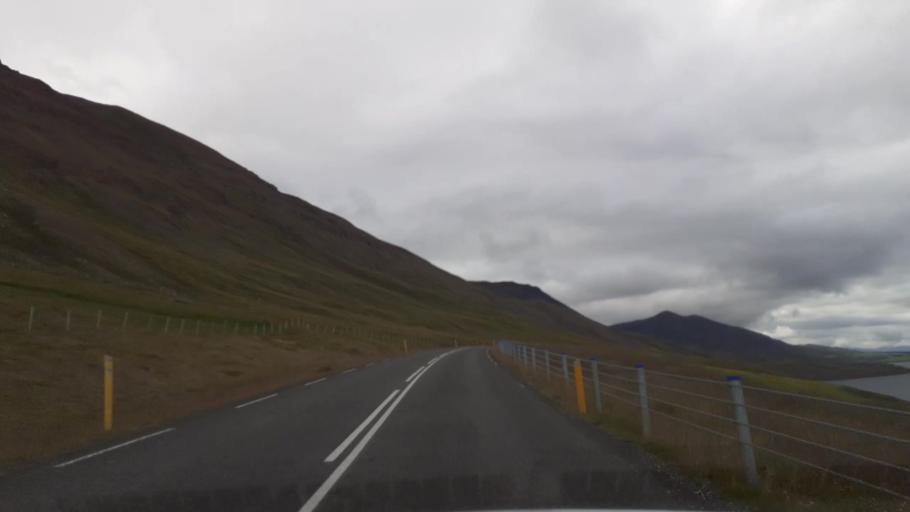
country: IS
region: Northeast
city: Akureyri
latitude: 65.8591
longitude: -18.0645
